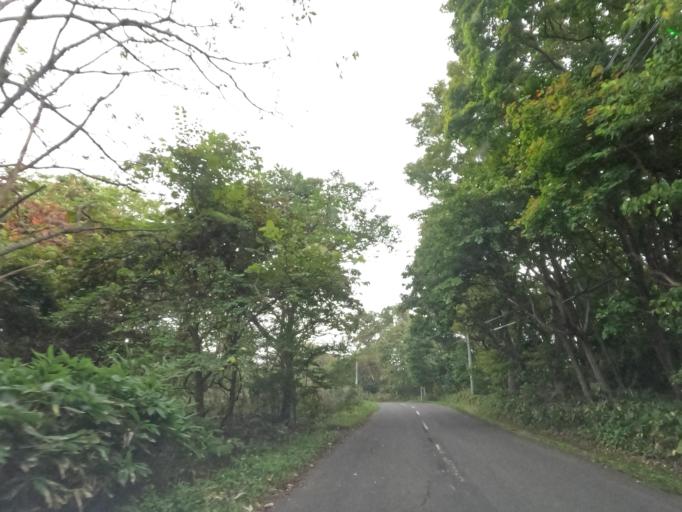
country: JP
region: Hokkaido
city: Date
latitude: 42.4110
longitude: 140.9157
